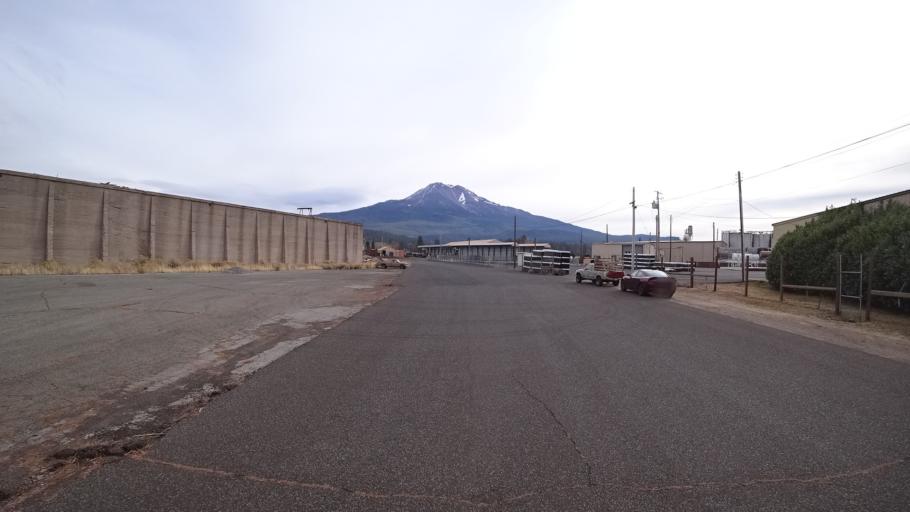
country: US
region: California
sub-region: Siskiyou County
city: Weed
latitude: 41.4342
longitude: -122.3746
